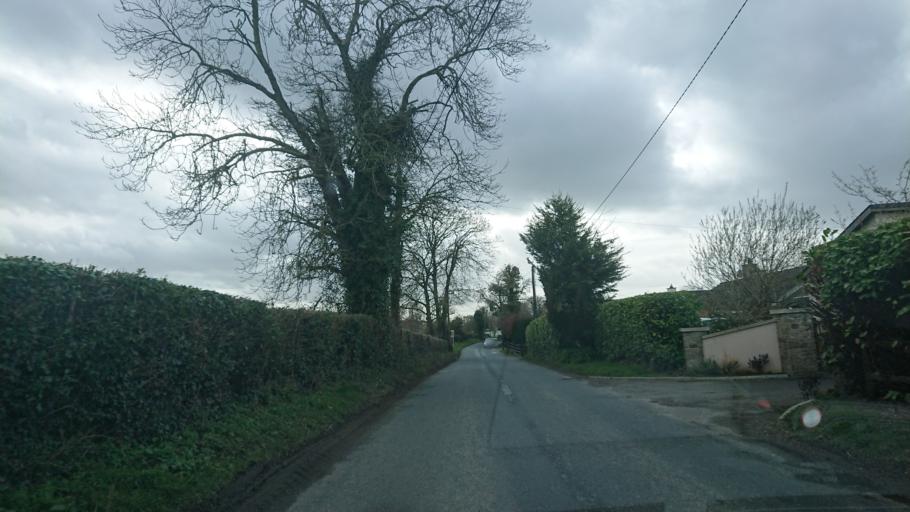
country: IE
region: Leinster
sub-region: Kildare
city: Naas
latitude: 53.1778
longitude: -6.6714
